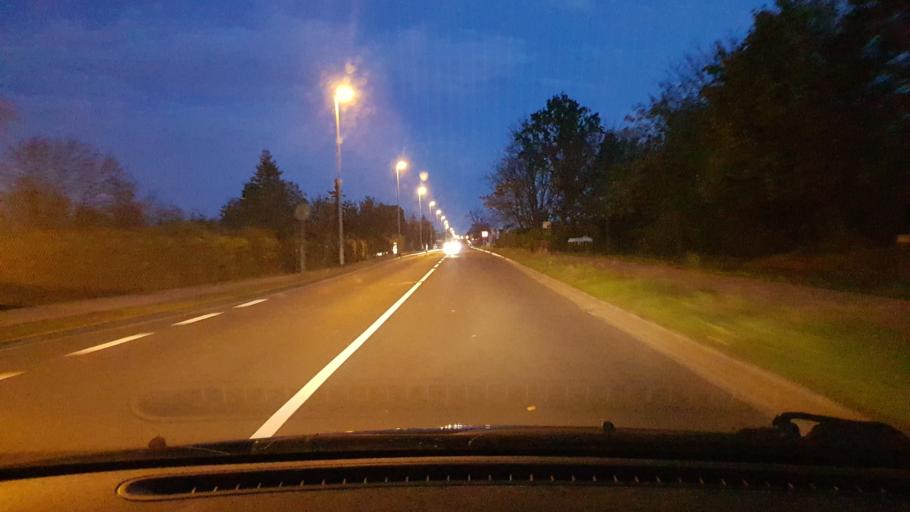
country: DE
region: Saxony-Anhalt
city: Rosslau
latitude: 51.8926
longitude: 12.2247
